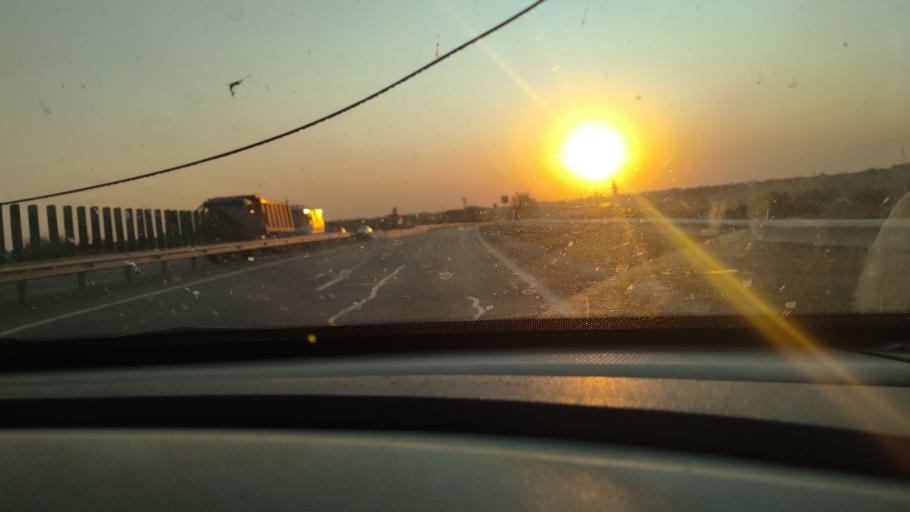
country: RU
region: Krasnodarskiy
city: Timashevsk
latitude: 45.6010
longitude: 38.9684
